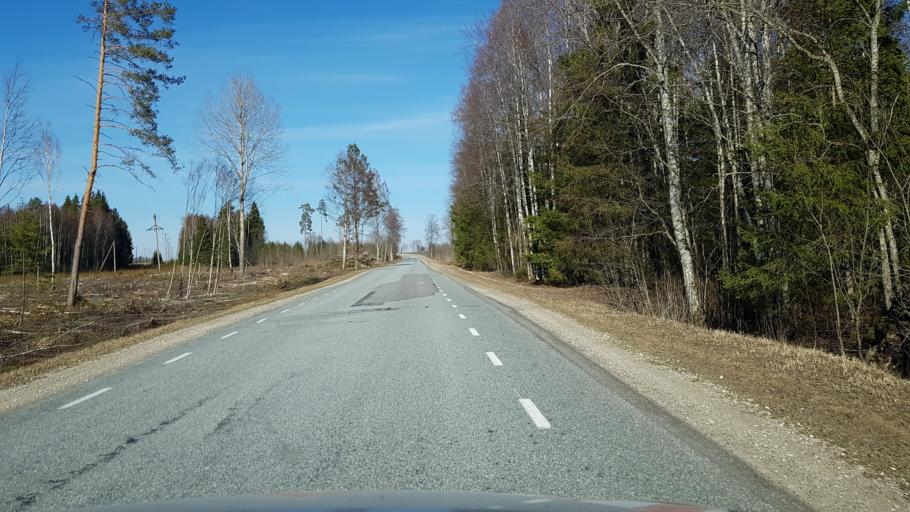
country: EE
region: Laeaene-Virumaa
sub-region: Rakke vald
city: Rakke
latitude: 59.0169
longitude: 26.3469
